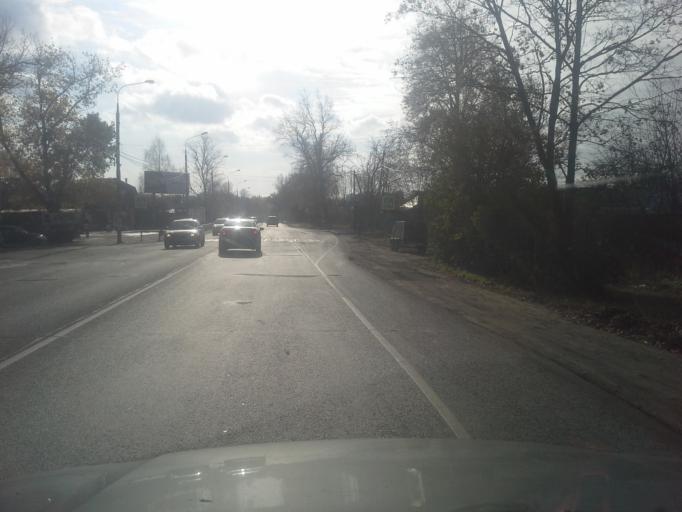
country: RU
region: Moskovskaya
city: Zvenigorod
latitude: 55.7224
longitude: 36.8635
